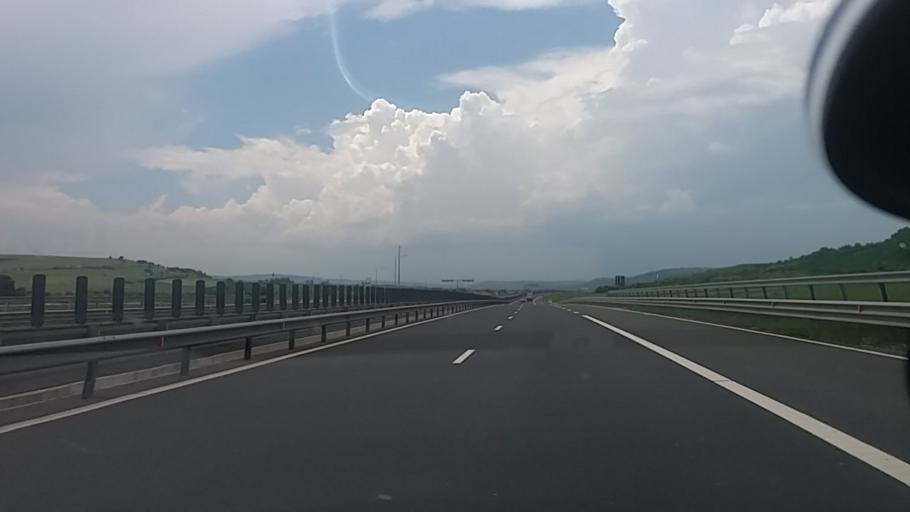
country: RO
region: Sibiu
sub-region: Comuna Apoldu de Jos
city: Apoldu de Jos
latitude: 45.8755
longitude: 23.8701
